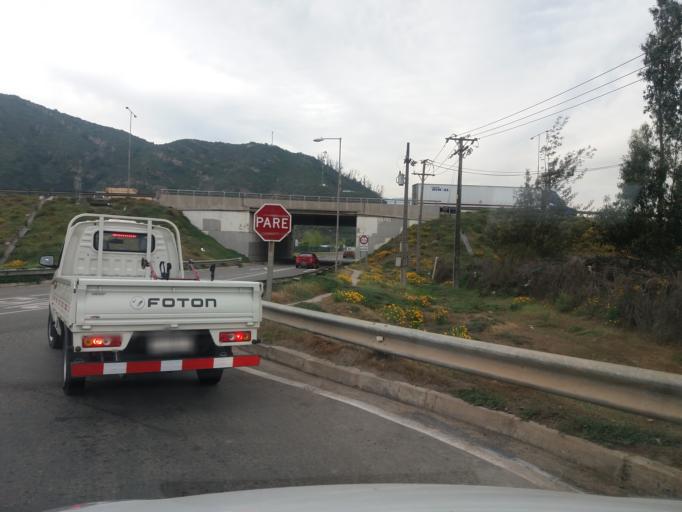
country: CL
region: Valparaiso
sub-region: Provincia de Quillota
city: Hacienda La Calera
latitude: -32.8427
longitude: -71.1093
